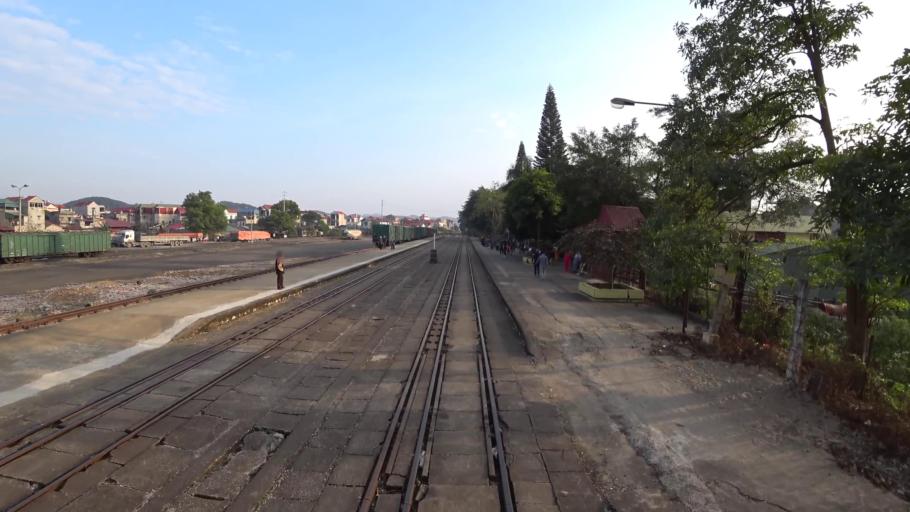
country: VN
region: Lang Son
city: Thi Tran Cao Loc
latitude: 21.8655
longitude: 106.7639
